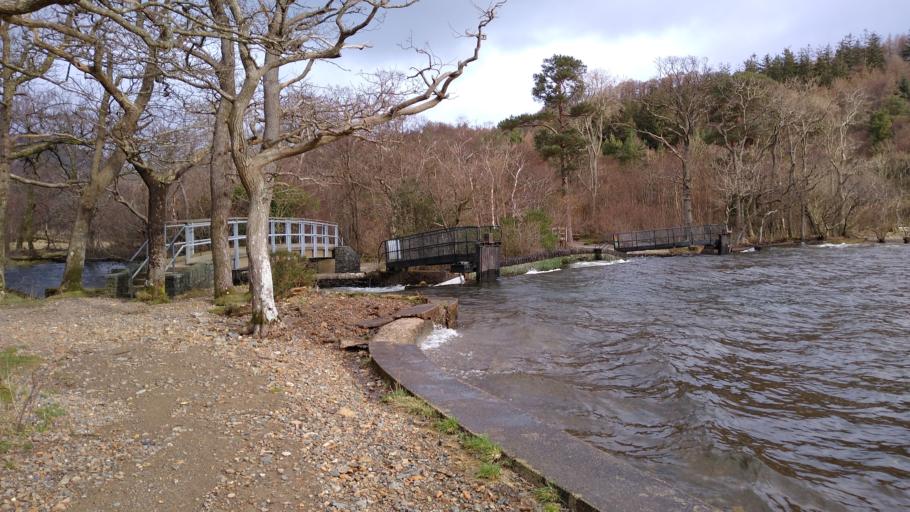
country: GB
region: England
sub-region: Cumbria
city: Cockermouth
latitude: 54.5752
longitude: -3.3147
